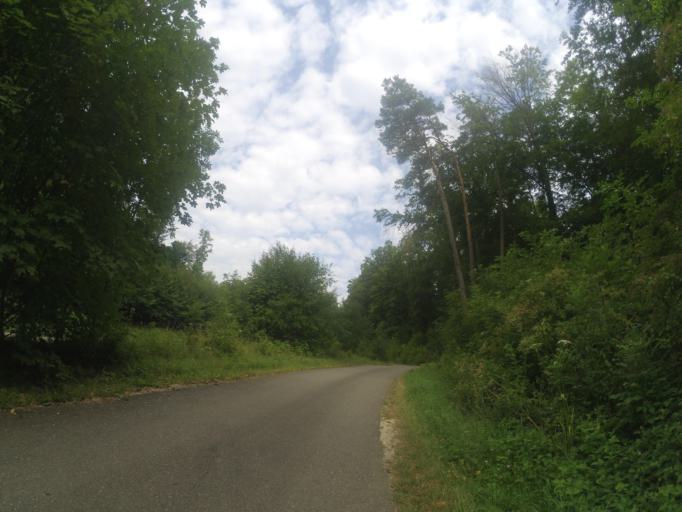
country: DE
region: Baden-Wuerttemberg
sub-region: Tuebingen Region
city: Lonsee
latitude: 48.5094
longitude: 9.9189
